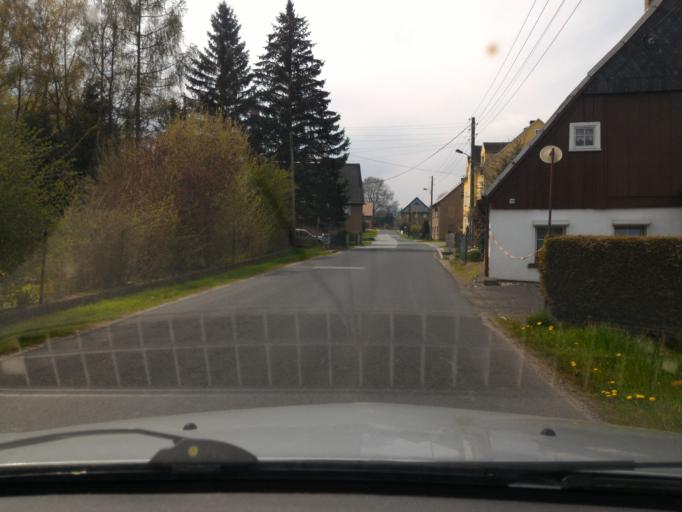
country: DE
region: Saxony
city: Hainewalde
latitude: 50.9170
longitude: 14.7136
